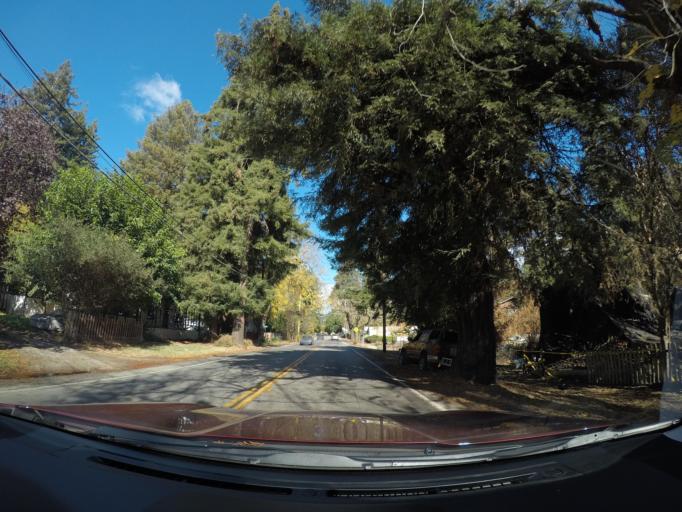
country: US
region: California
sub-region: Santa Cruz County
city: Boulder Creek
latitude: 37.1191
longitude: -122.1208
